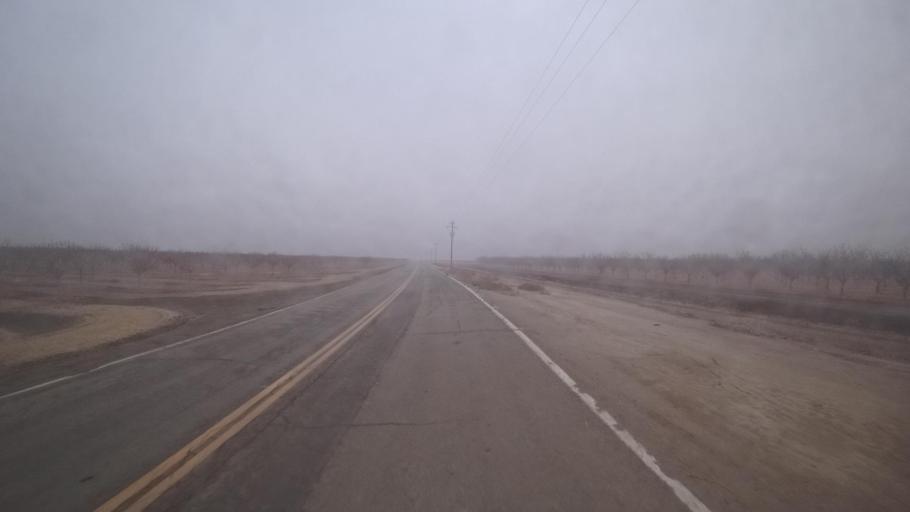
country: US
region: California
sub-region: Kern County
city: Buttonwillow
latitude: 35.4269
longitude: -119.5361
